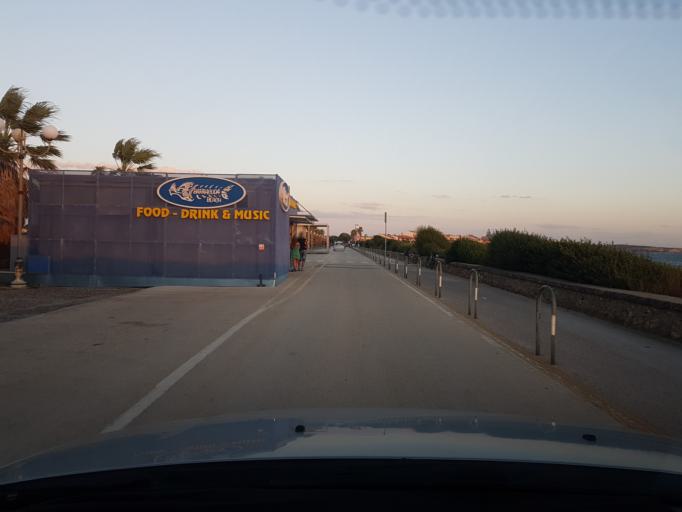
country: IT
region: Sardinia
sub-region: Provincia di Oristano
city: Riola Sardo
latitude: 40.0306
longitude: 8.4053
